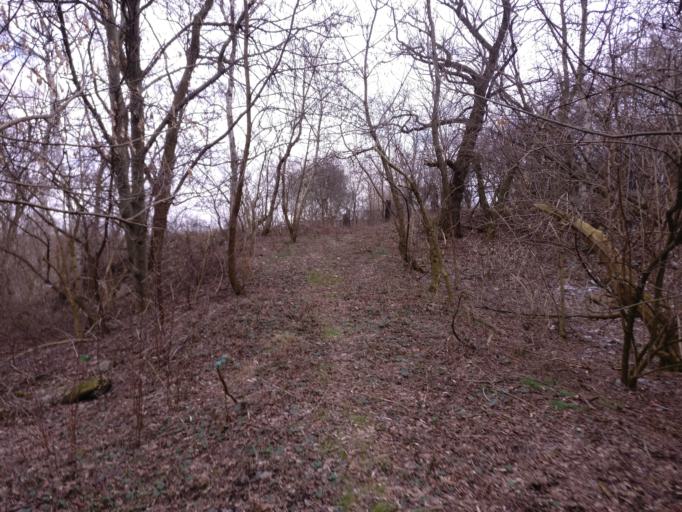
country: PL
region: Silesian Voivodeship
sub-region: Powiat bedzinski
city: Bedzin
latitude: 50.3004
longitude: 19.1746
